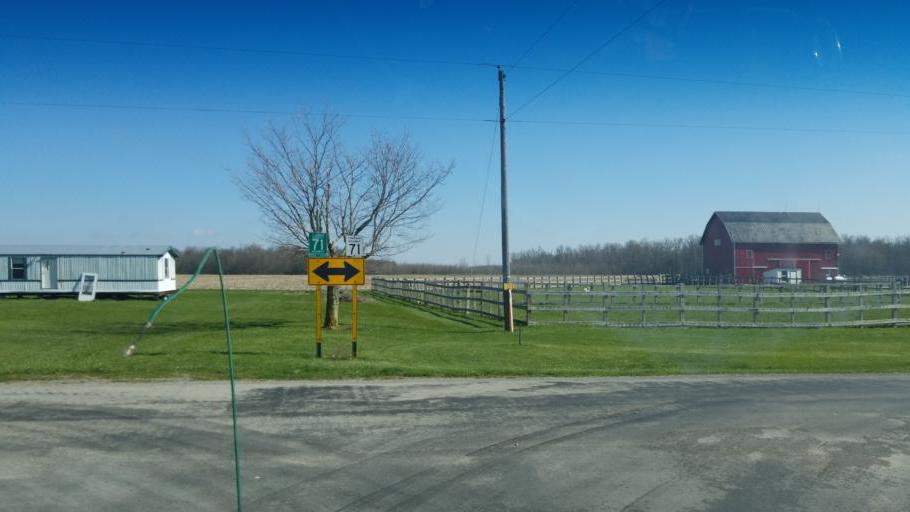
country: US
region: Ohio
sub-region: Hardin County
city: Forest
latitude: 40.7167
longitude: -83.4453
